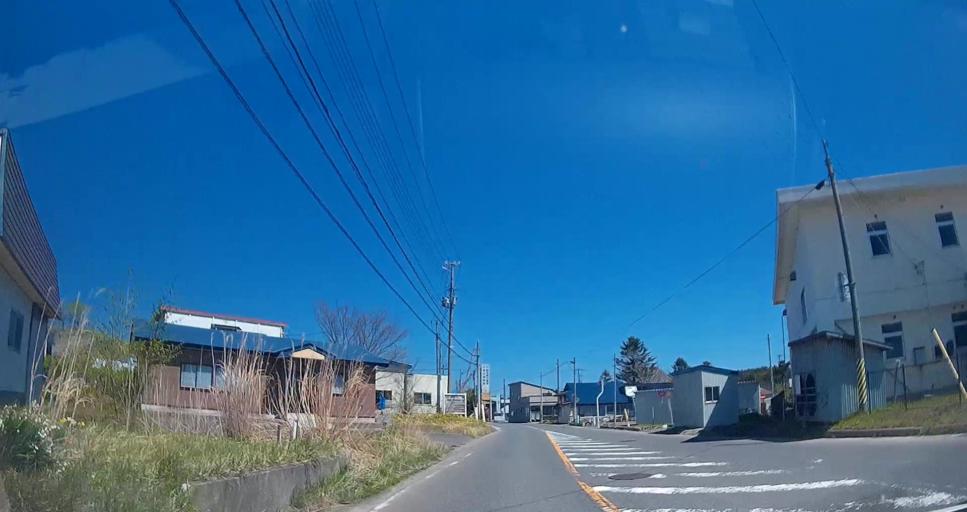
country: JP
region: Aomori
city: Misawa
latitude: 40.9604
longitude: 141.3728
